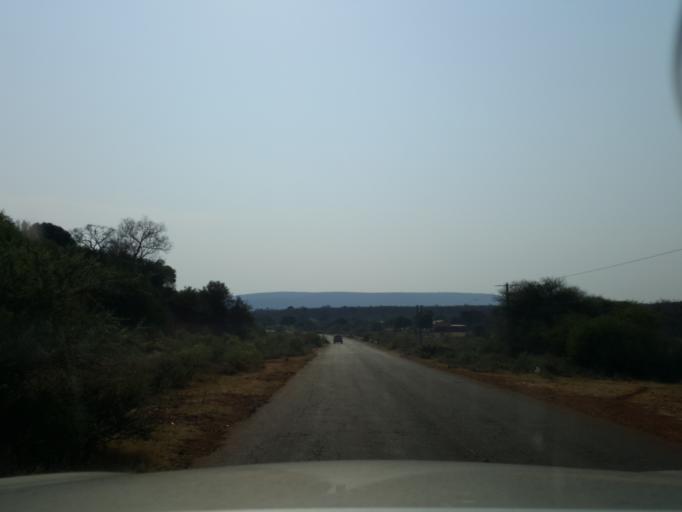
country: BW
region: South East
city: Lobatse
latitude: -25.3038
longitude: 25.8245
